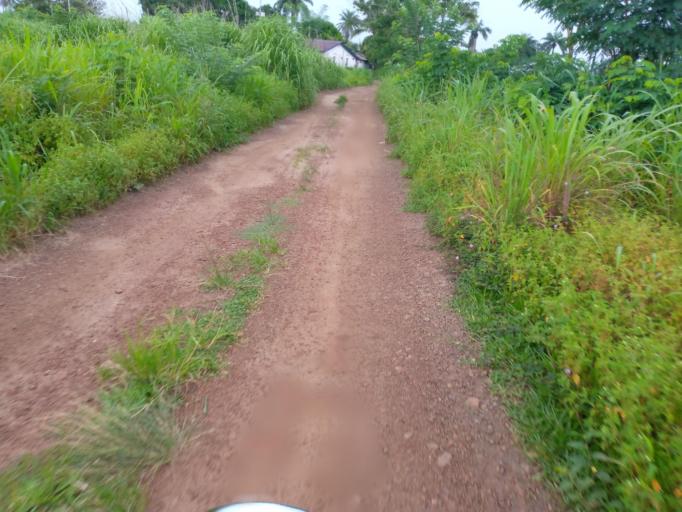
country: SL
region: Southern Province
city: Moyamba
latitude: 8.1489
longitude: -12.4370
